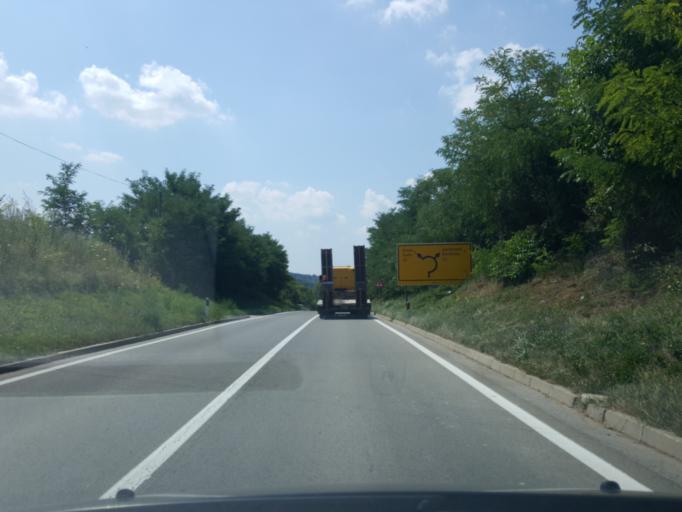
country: RS
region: Central Serbia
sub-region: Sumadijski Okrug
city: Topola
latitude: 44.2906
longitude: 20.6950
